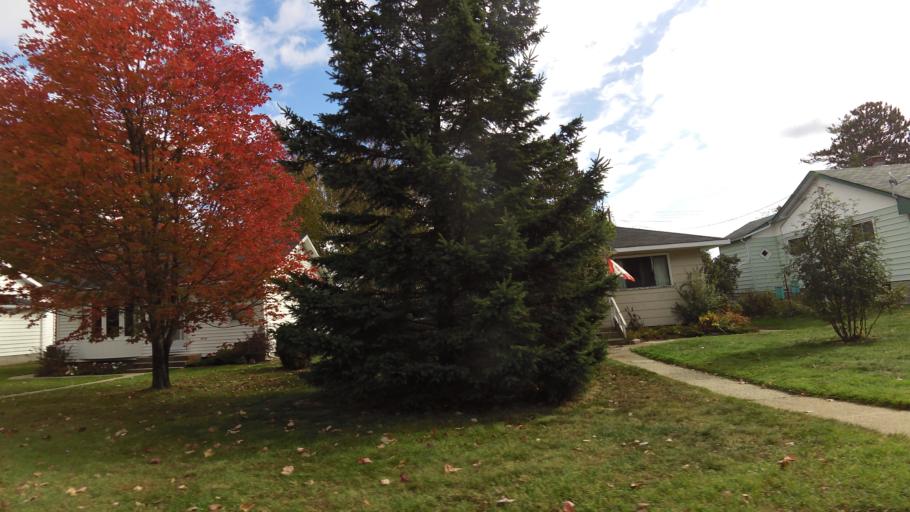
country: CA
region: Ontario
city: Deep River
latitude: 46.0987
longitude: -77.4885
